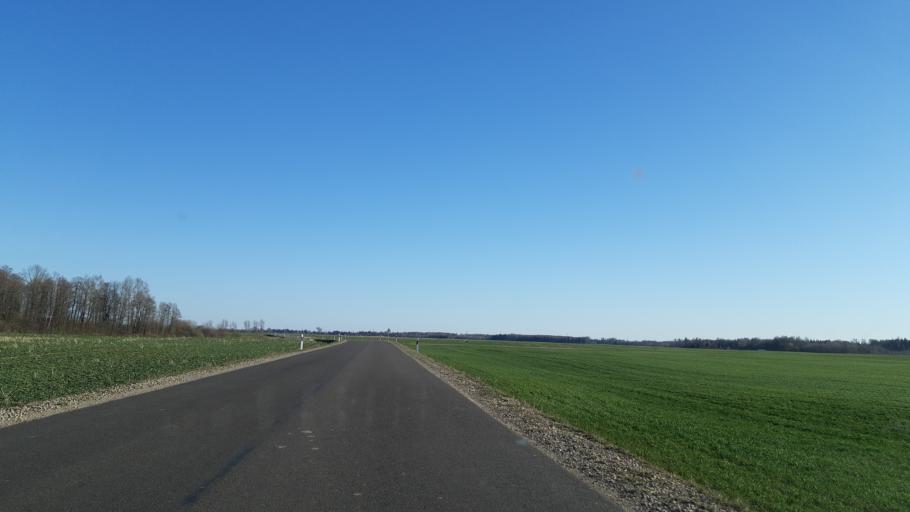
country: LT
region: Kauno apskritis
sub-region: Kauno rajonas
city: Akademija (Kaunas)
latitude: 55.0239
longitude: 23.7617
